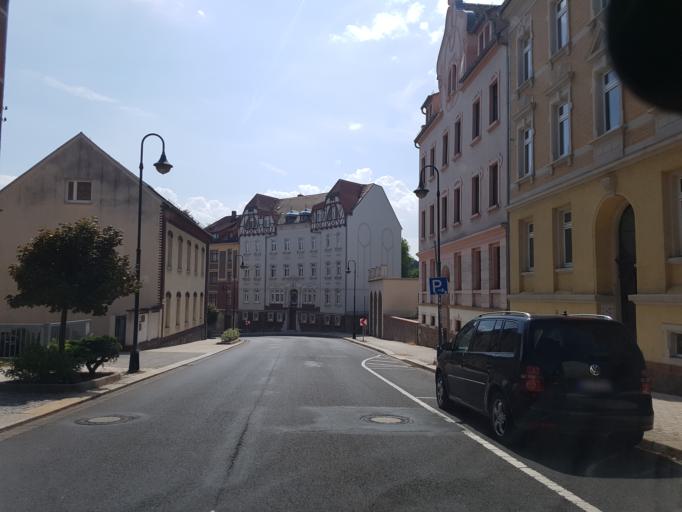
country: DE
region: Saxony
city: Waldheim
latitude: 51.0720
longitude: 13.0190
